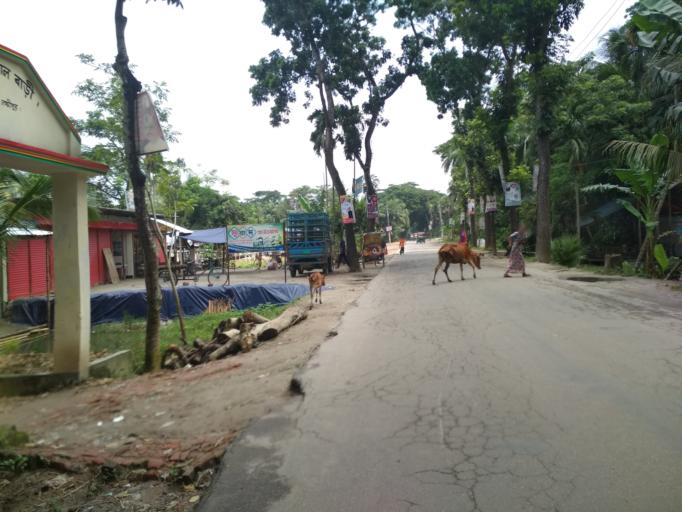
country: BD
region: Chittagong
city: Lakshmipur
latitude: 22.9482
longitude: 90.8086
